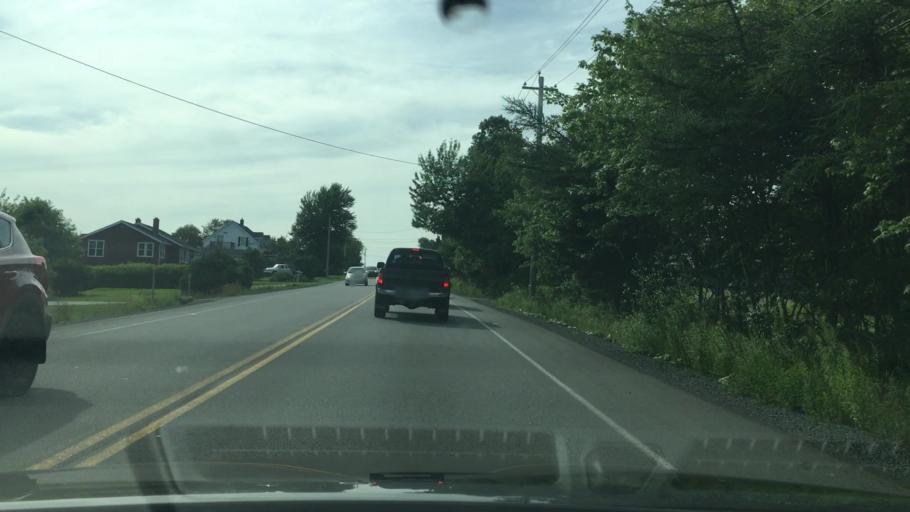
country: CA
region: Nova Scotia
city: Dartmouth
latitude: 44.7298
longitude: -63.7516
